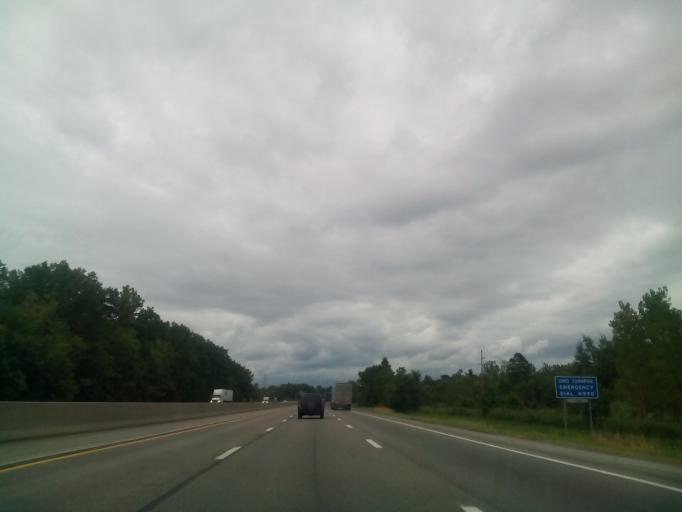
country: US
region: Ohio
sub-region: Lorain County
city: South Amherst
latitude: 41.3693
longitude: -82.2703
